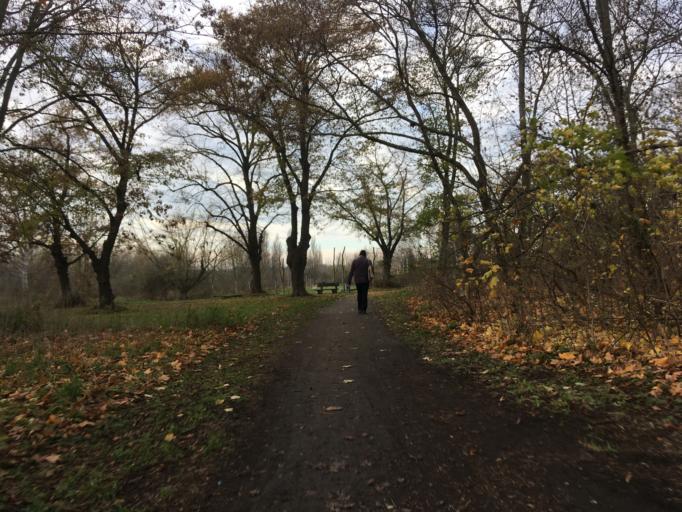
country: DE
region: Berlin
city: Falkenberg
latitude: 52.5670
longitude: 13.5442
